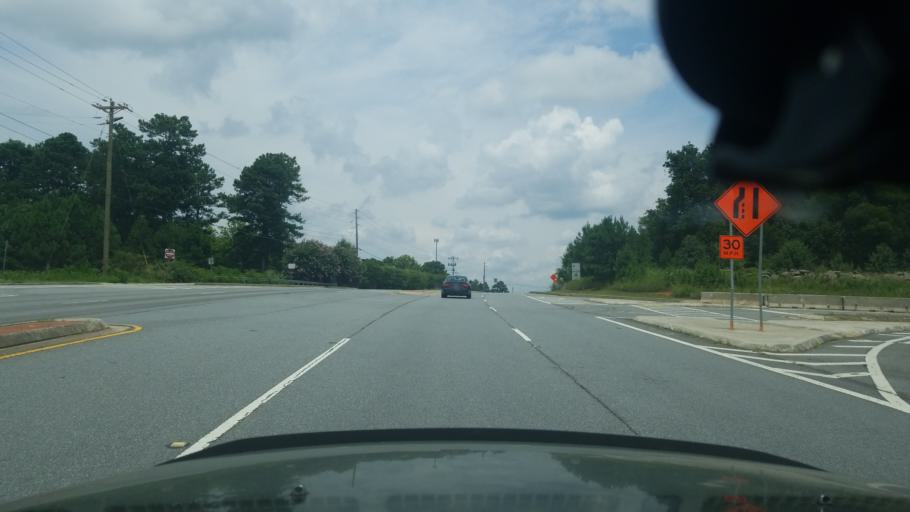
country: US
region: Georgia
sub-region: Fulton County
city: Alpharetta
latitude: 34.1044
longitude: -84.2367
